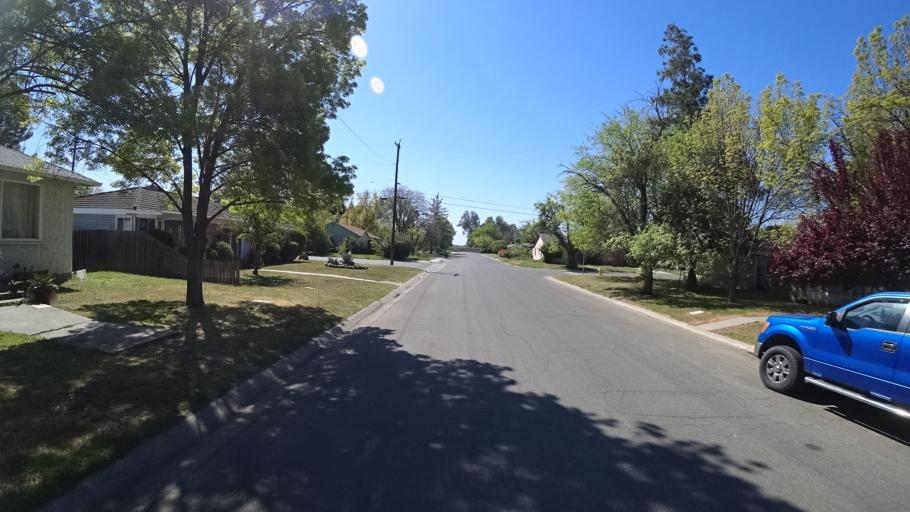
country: US
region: California
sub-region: Glenn County
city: Willows
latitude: 39.5196
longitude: -122.1882
